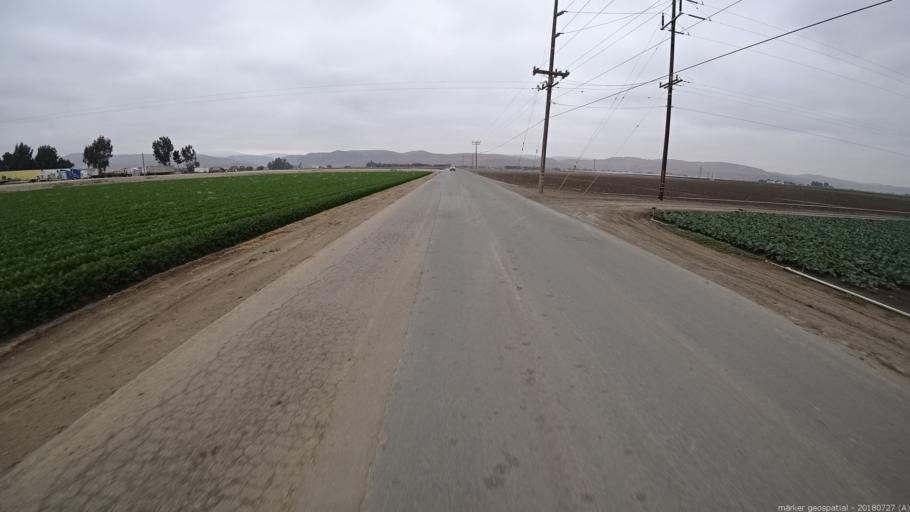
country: US
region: California
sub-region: Monterey County
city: Greenfield
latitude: 36.3284
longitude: -121.2219
